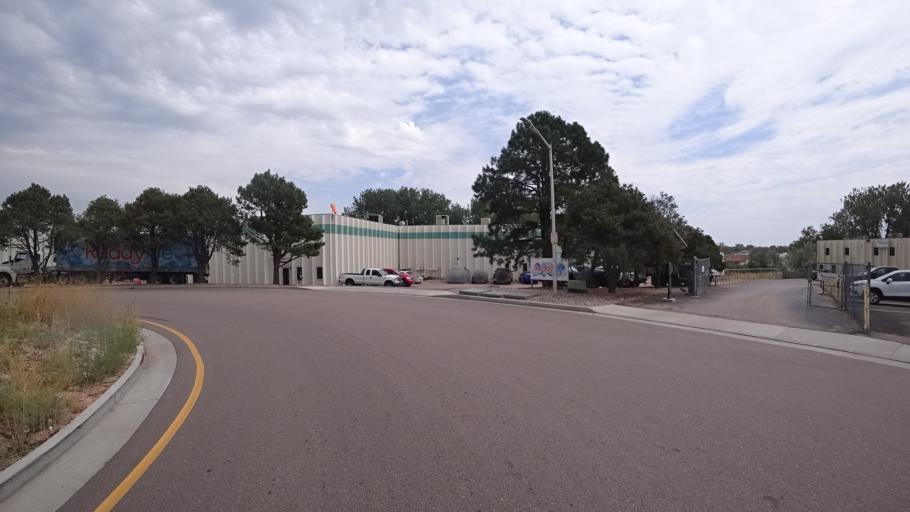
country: US
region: Colorado
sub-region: El Paso County
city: Colorado Springs
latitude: 38.8942
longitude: -104.8284
